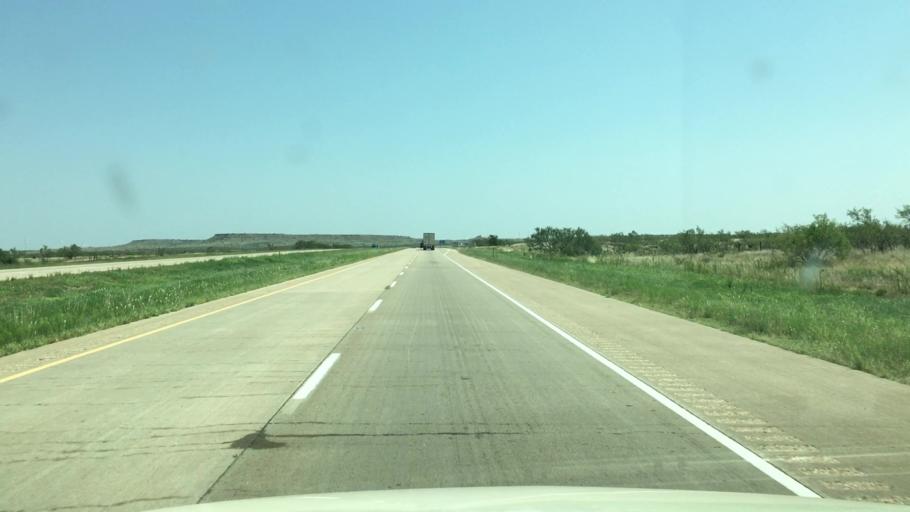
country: US
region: Texas
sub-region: Oldham County
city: Vega
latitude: 35.2358
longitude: -102.8405
